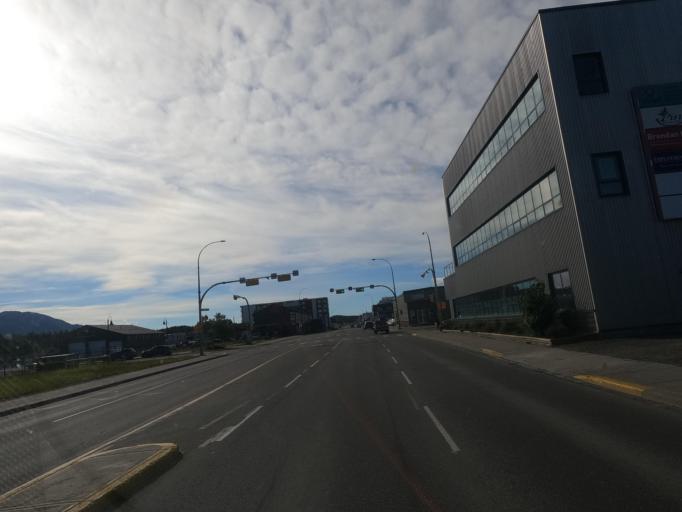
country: CA
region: Yukon
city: Whitehorse
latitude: 60.7247
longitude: -135.0562
